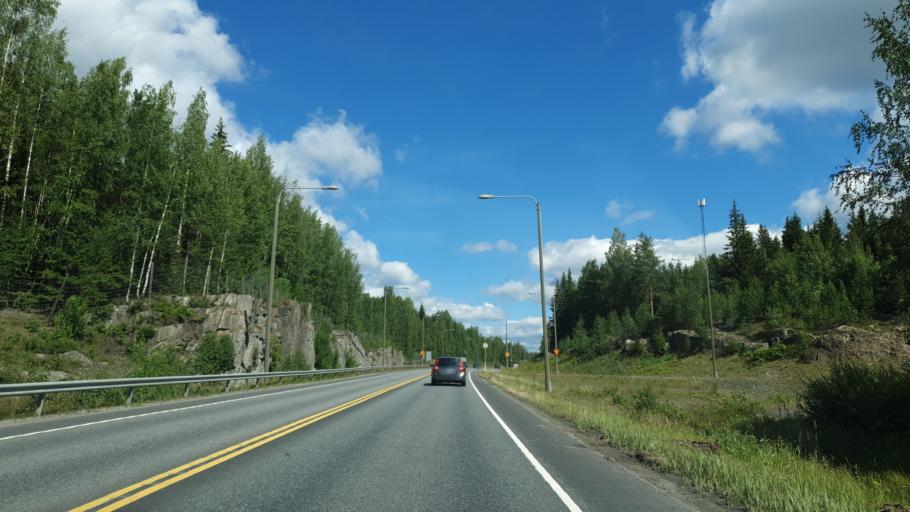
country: FI
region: Pirkanmaa
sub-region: Tampere
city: Kangasala
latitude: 61.5330
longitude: 23.9527
